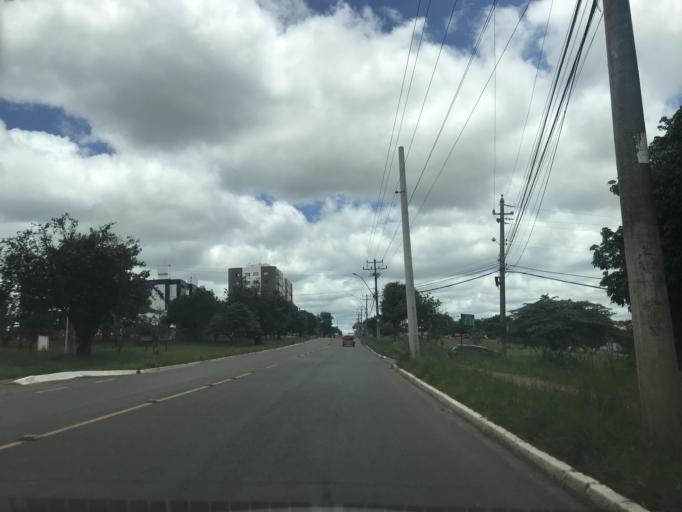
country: BR
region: Federal District
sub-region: Brasilia
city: Brasilia
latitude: -15.6537
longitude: -47.7925
